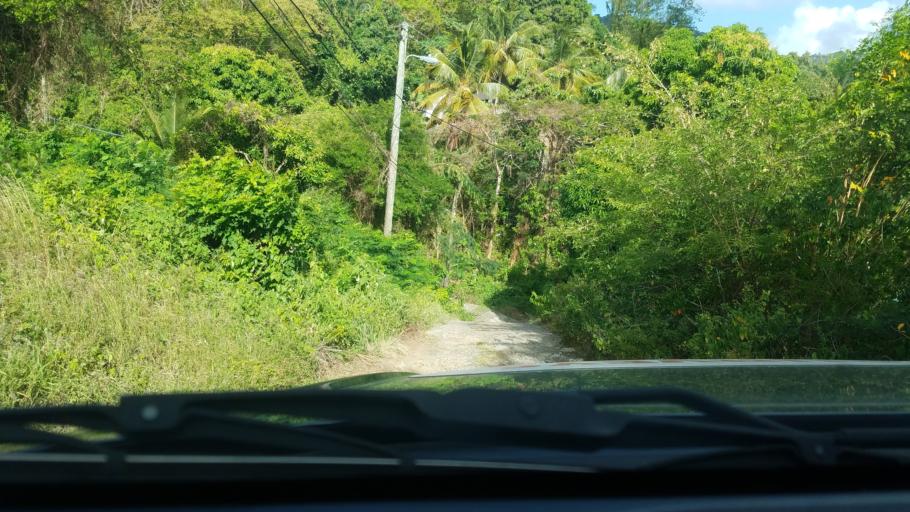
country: LC
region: Gros-Islet
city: Gros Islet
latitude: 14.0388
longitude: -60.9499
